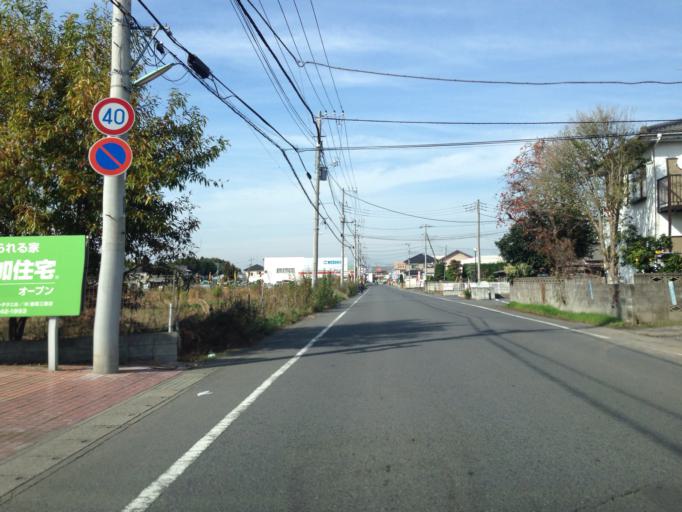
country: JP
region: Ibaraki
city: Naka
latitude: 36.0368
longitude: 140.1602
